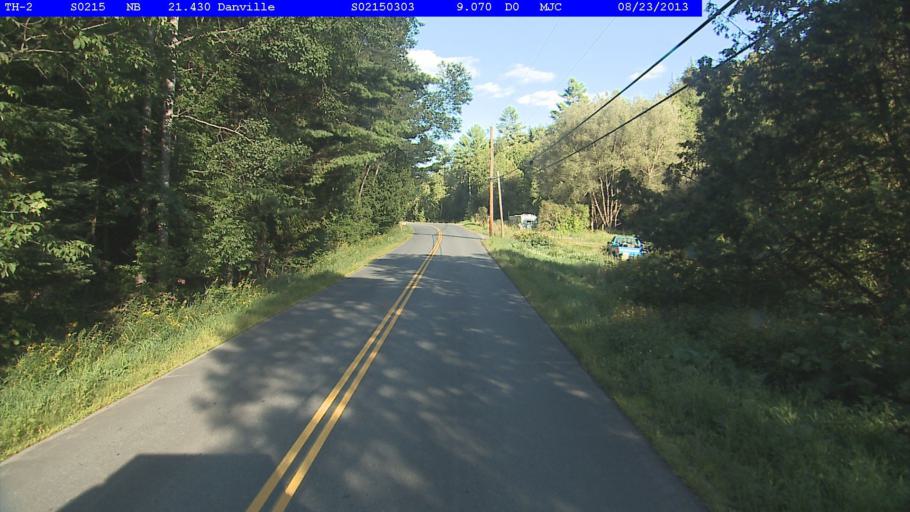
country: US
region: Vermont
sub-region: Caledonia County
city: St Johnsbury
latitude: 44.4558
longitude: -72.0820
